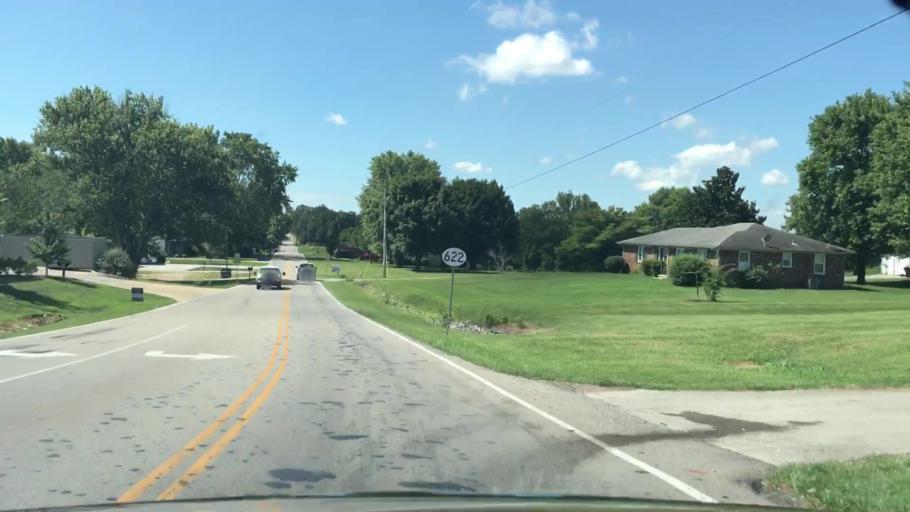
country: US
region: Kentucky
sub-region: Warren County
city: Plano
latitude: 36.9197
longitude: -86.4092
